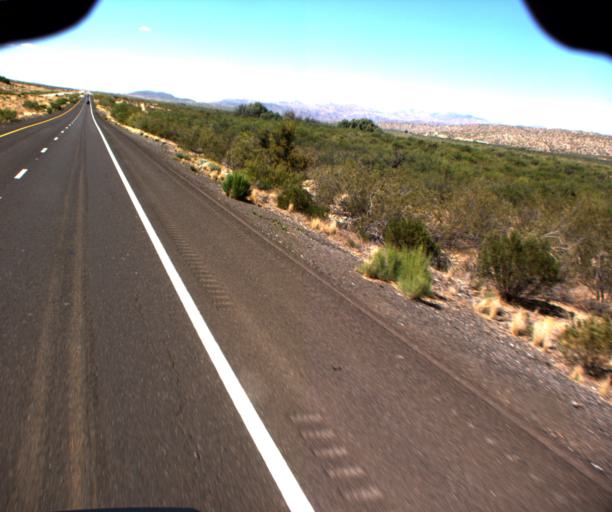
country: US
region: Arizona
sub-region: Yavapai County
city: Bagdad
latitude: 34.8398
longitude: -113.6340
